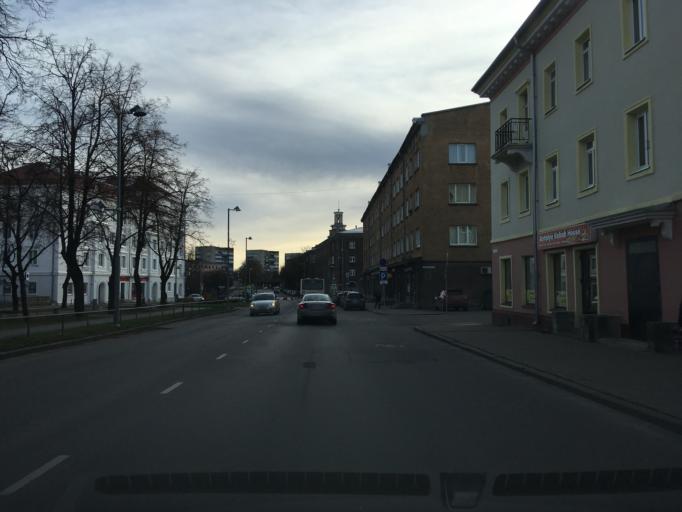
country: EE
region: Ida-Virumaa
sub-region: Narva linn
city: Narva
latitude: 59.3747
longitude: 28.1945
